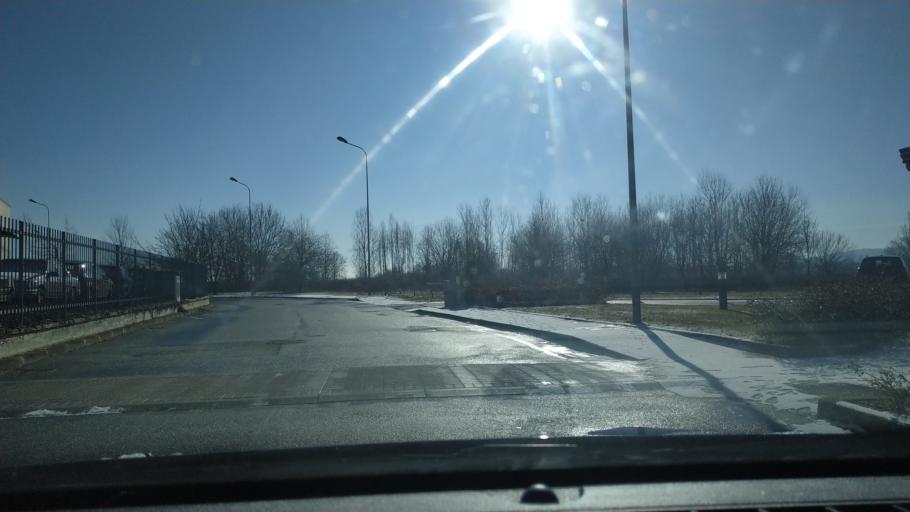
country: IT
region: Piedmont
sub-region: Provincia di Torino
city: Samone
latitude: 45.4455
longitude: 7.8336
